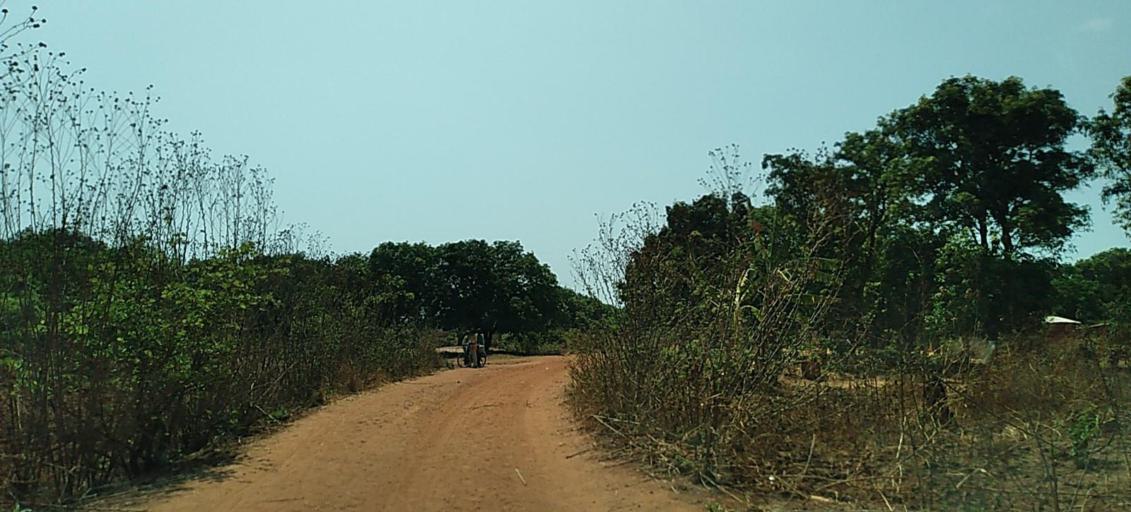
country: ZM
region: Copperbelt
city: Luanshya
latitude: -13.3491
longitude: 28.4029
